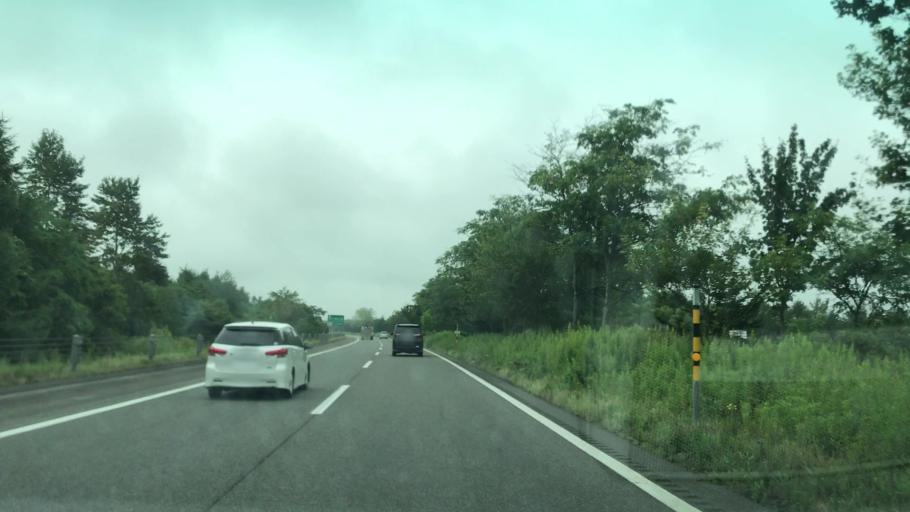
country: JP
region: Hokkaido
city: Chitose
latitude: 42.7853
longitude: 141.6263
